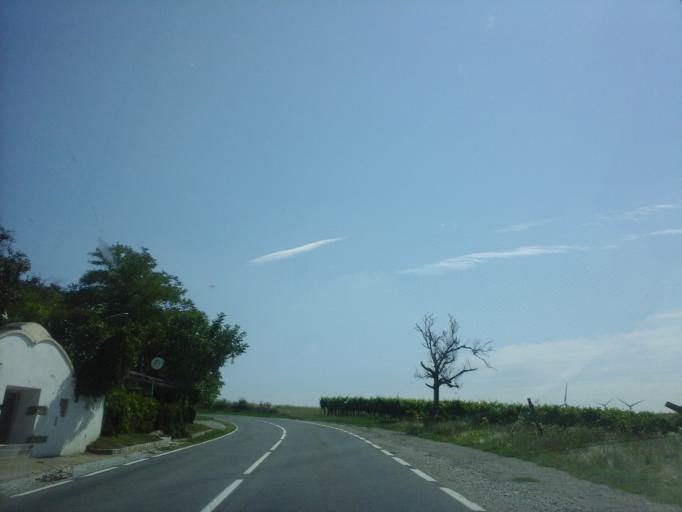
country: AT
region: Burgenland
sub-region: Politischer Bezirk Neusiedl am See
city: Edelstal
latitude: 48.0873
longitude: 16.9846
